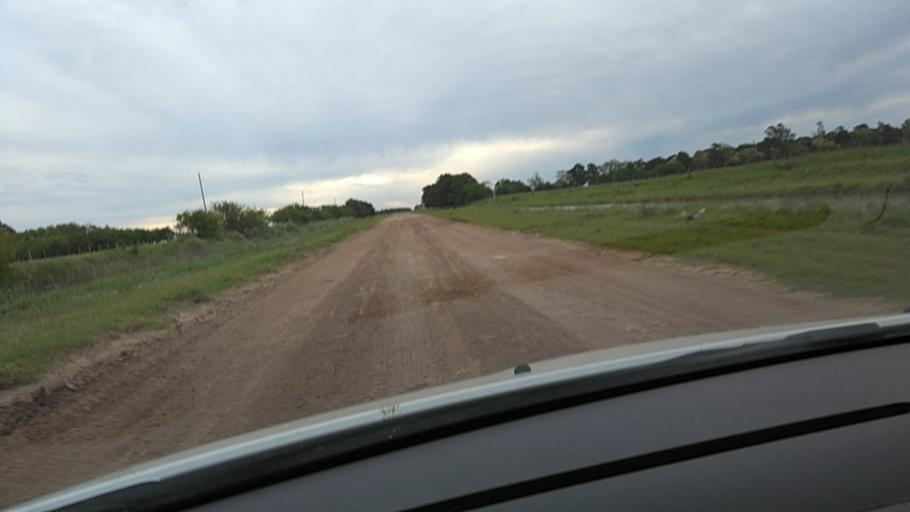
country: AR
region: Buenos Aires
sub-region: Partido de General Madariaga
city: General Juan Madariaga
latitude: -36.9663
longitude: -57.1832
